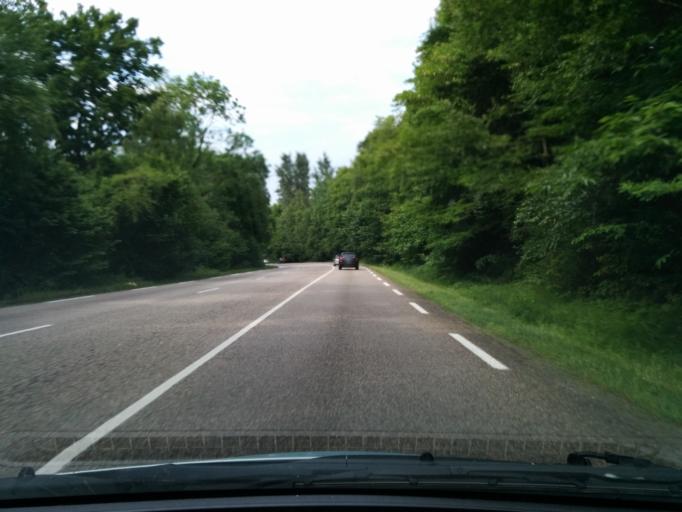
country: FR
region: Haute-Normandie
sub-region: Departement de l'Eure
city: Saint-Aubin-sur-Gaillon
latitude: 49.1440
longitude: 1.3195
